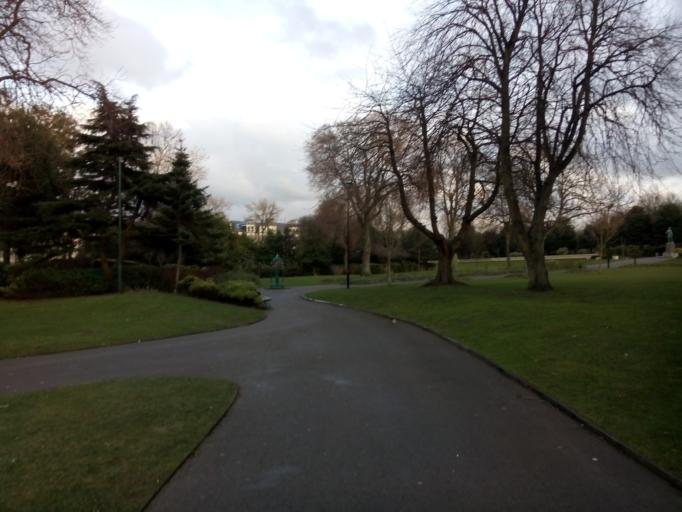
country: GB
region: England
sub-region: Sunderland
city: Sunderland
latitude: 54.9034
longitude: -1.3806
